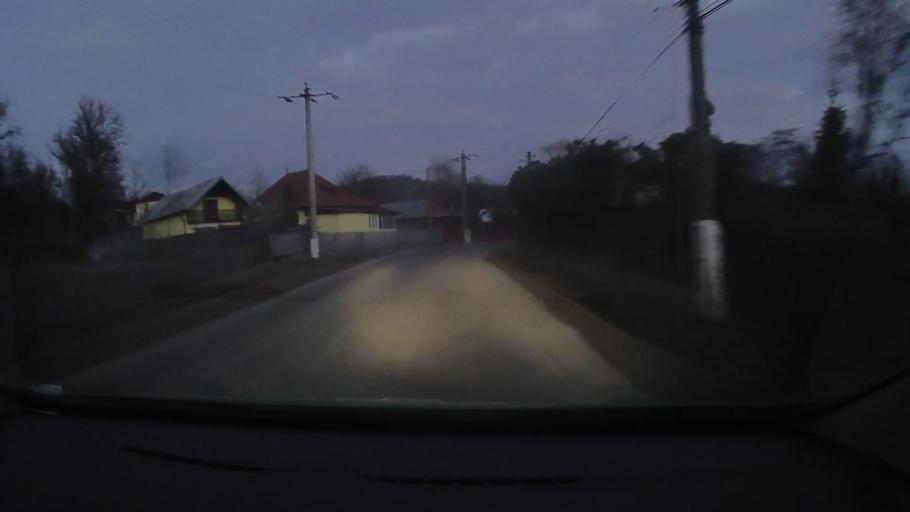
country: RO
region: Prahova
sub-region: Comuna Provita de Jos
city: Provita de Jos
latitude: 45.1201
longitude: 25.6658
